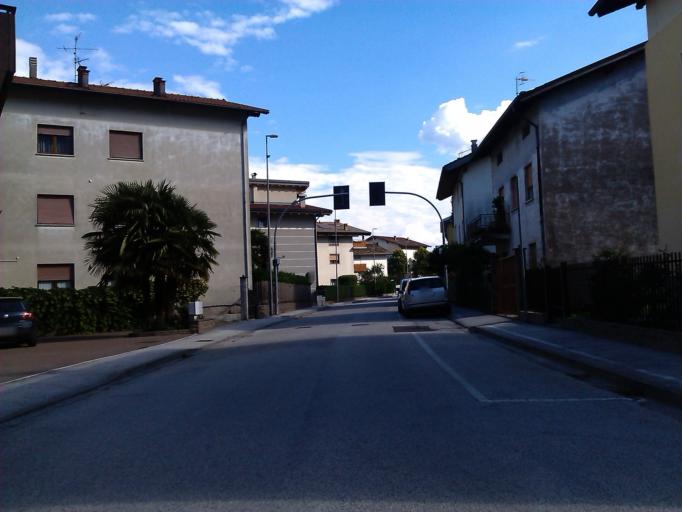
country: IT
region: Trentino-Alto Adige
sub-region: Provincia di Trento
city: Zambana
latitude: 46.1528
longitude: 11.0954
